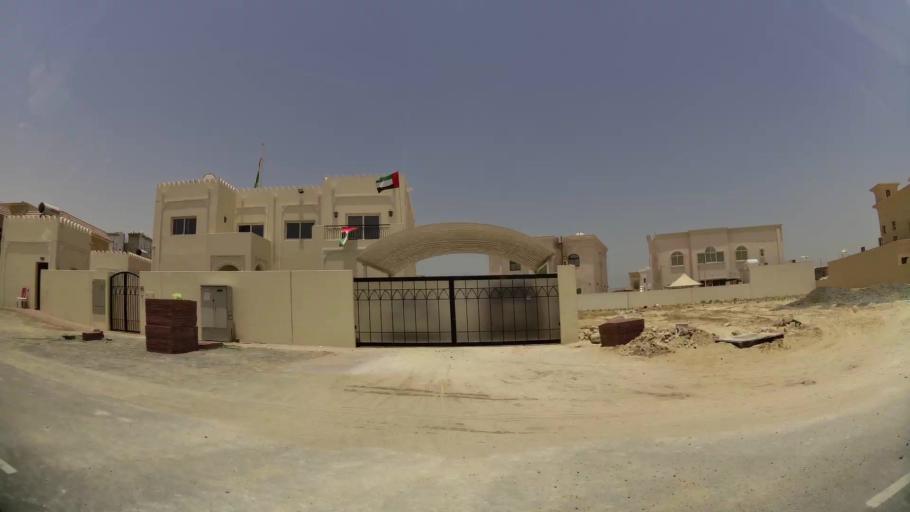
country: AE
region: Dubai
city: Dubai
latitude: 25.0931
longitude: 55.2301
